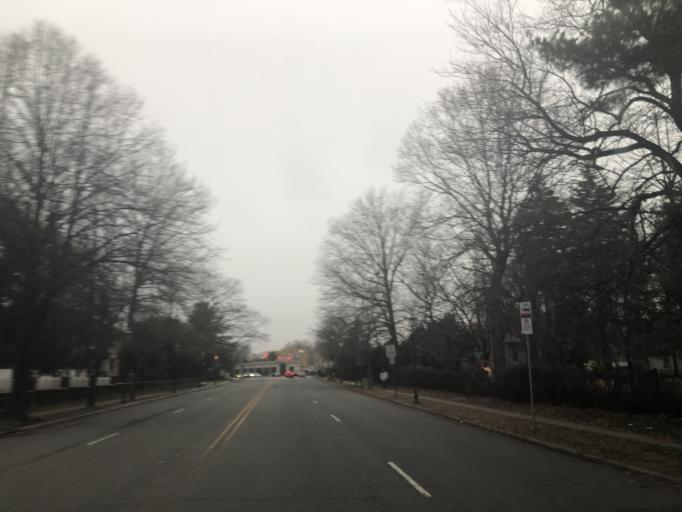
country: US
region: New Jersey
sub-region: Essex County
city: Irvington
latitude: 40.7457
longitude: -74.2401
